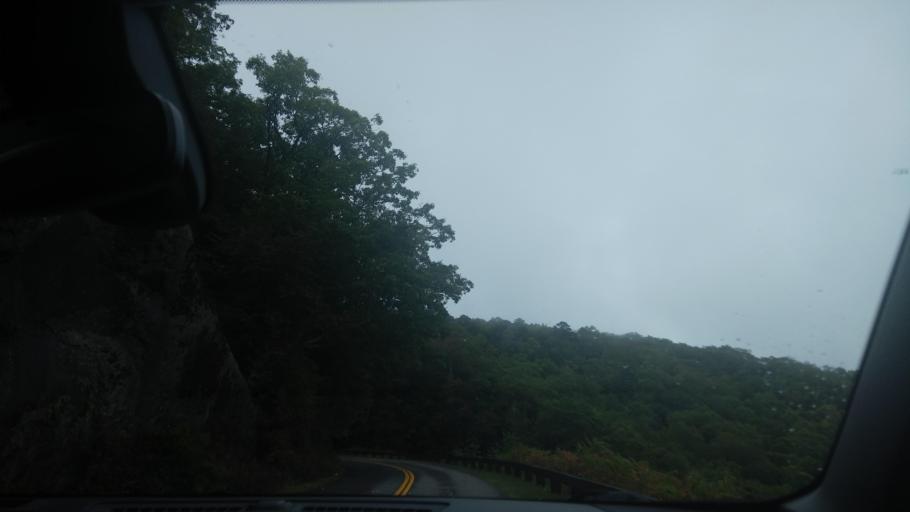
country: US
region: North Carolina
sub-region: Mitchell County
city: Spruce Pine
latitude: 35.9038
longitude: -81.9679
